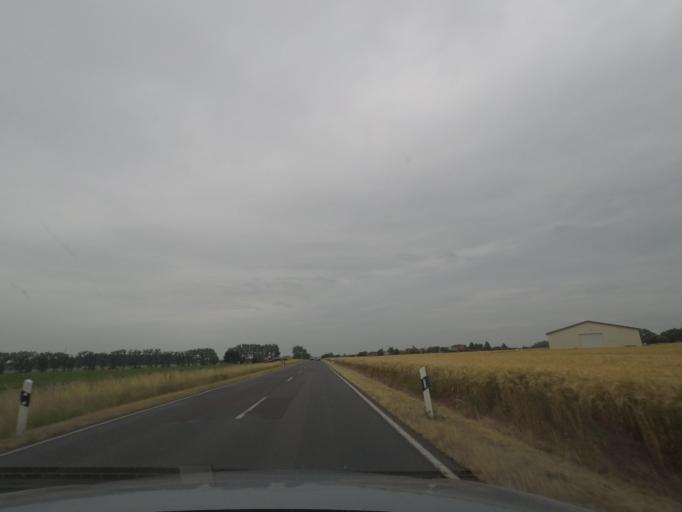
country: DE
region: Saxony-Anhalt
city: Oschersleben
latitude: 52.0454
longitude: 11.2645
